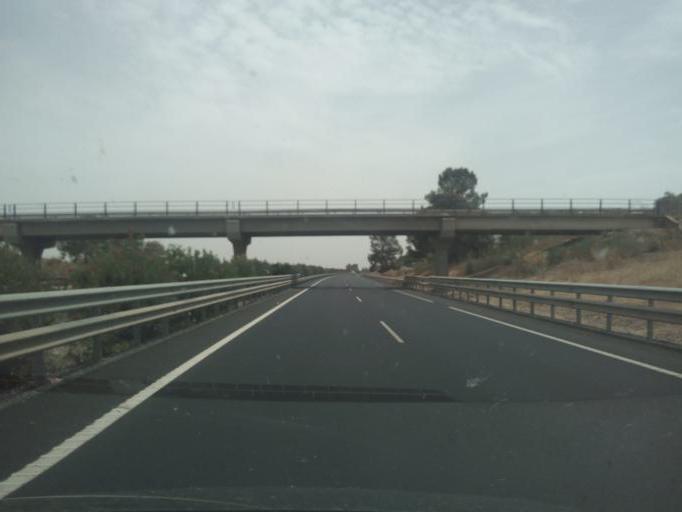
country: ES
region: Andalusia
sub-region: Provincia de Huelva
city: Bollullos par del Condado
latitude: 37.3599
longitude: -6.5161
